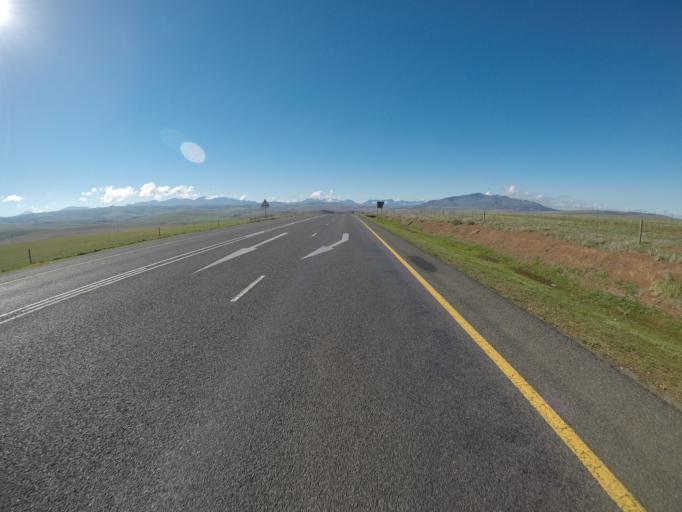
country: ZA
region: Western Cape
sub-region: Overberg District Municipality
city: Caledon
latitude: -34.2186
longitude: 19.3150
